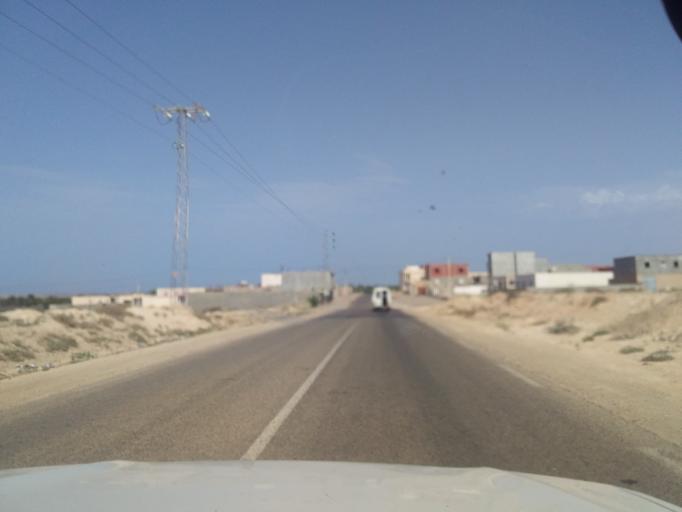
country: TN
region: Qabis
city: Gabes
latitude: 33.6416
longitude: 10.2938
